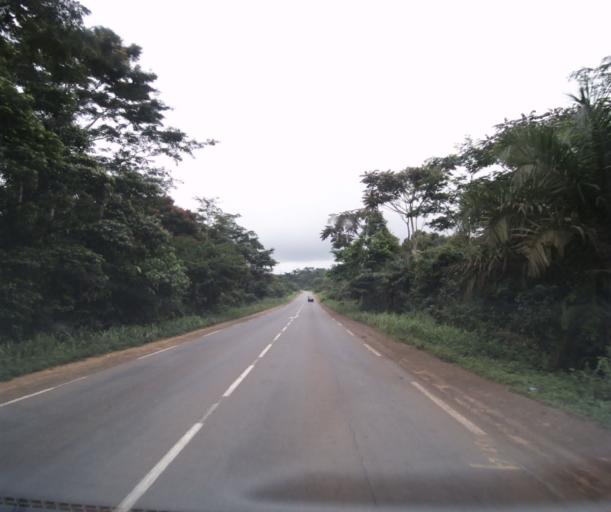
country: CM
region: Centre
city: Mbankomo
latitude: 3.7817
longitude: 11.2747
